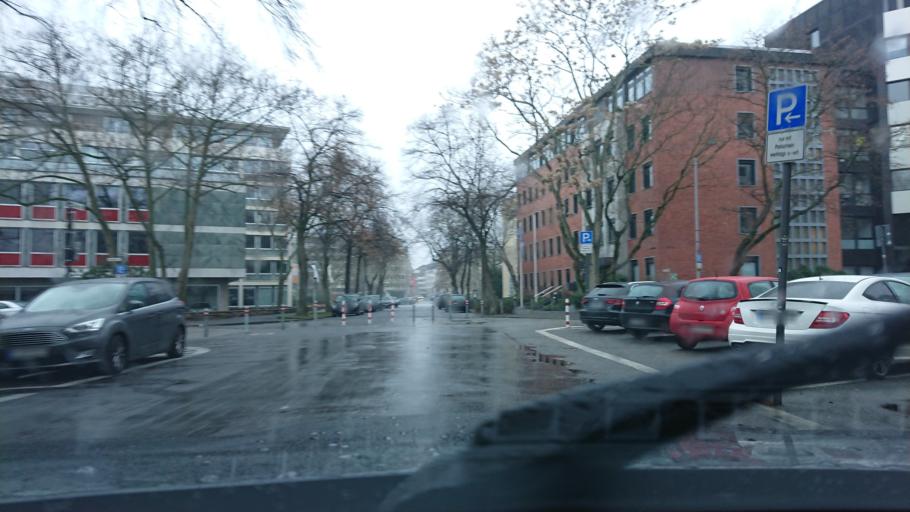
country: DE
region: North Rhine-Westphalia
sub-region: Regierungsbezirk Koln
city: Altstadt Nord
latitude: 50.9518
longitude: 6.9642
